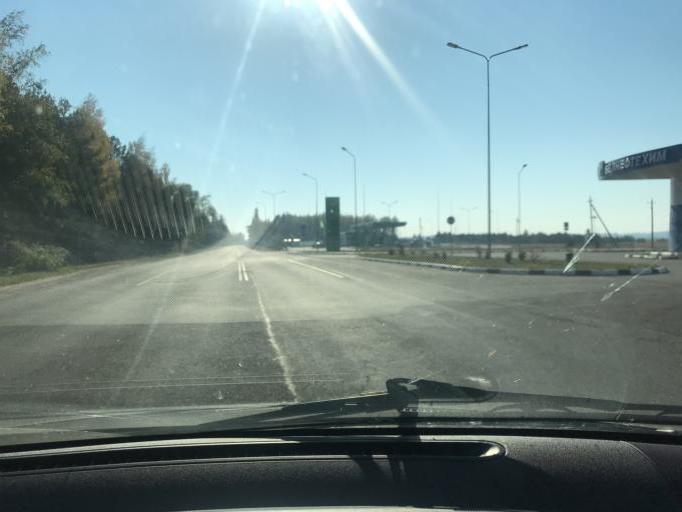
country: BY
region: Brest
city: Davyd-Haradok
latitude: 52.2475
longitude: 27.0838
